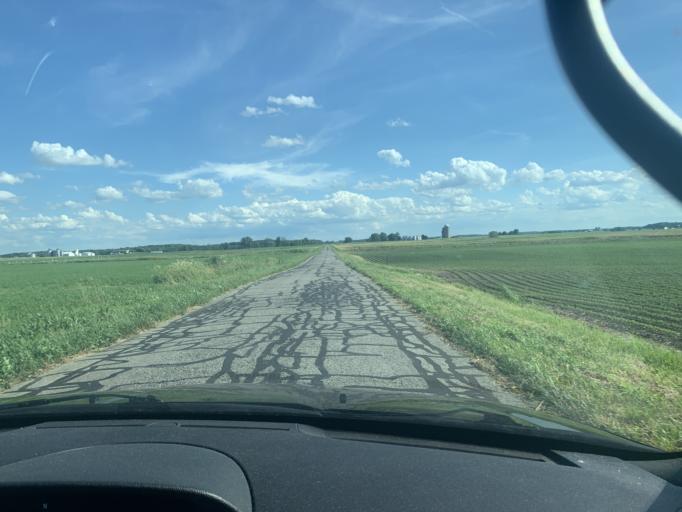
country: US
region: Ohio
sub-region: Logan County
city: De Graff
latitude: 40.3332
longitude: -83.8725
